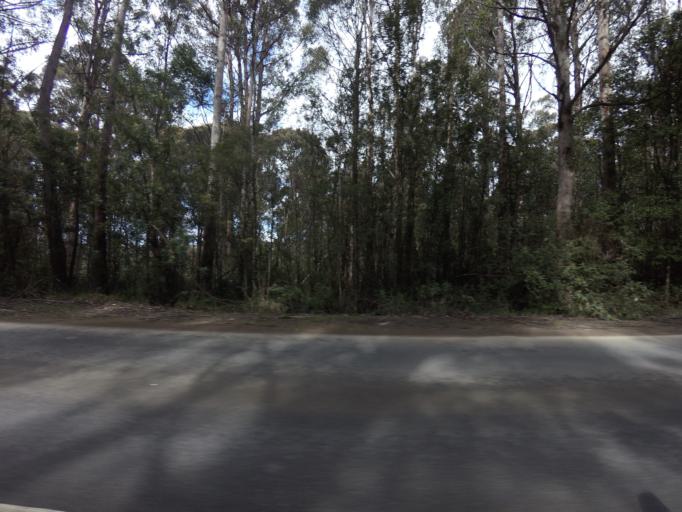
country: AU
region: Tasmania
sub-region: Huon Valley
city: Geeveston
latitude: -43.3403
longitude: 146.9706
